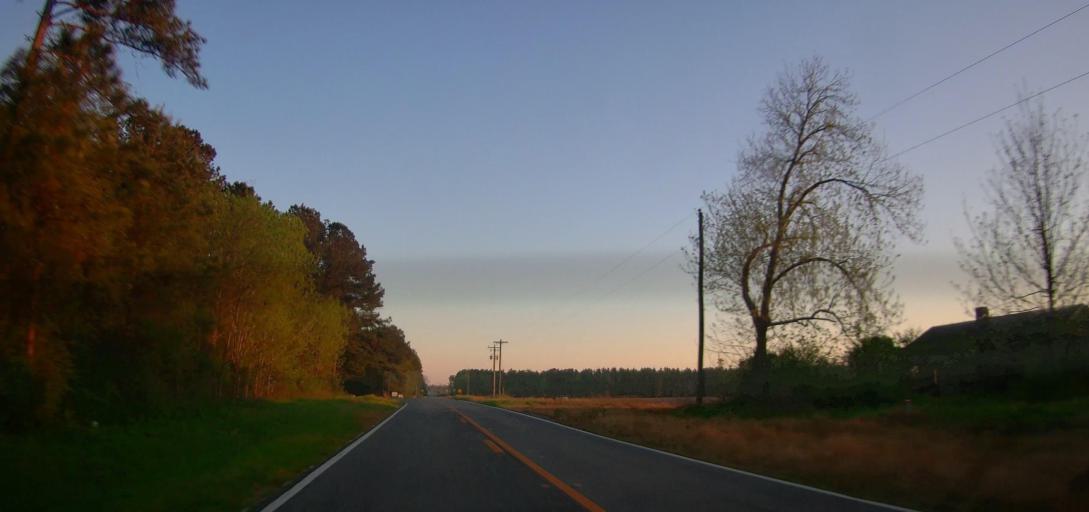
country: US
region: Georgia
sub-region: Ben Hill County
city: Fitzgerald
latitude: 31.7744
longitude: -83.3845
